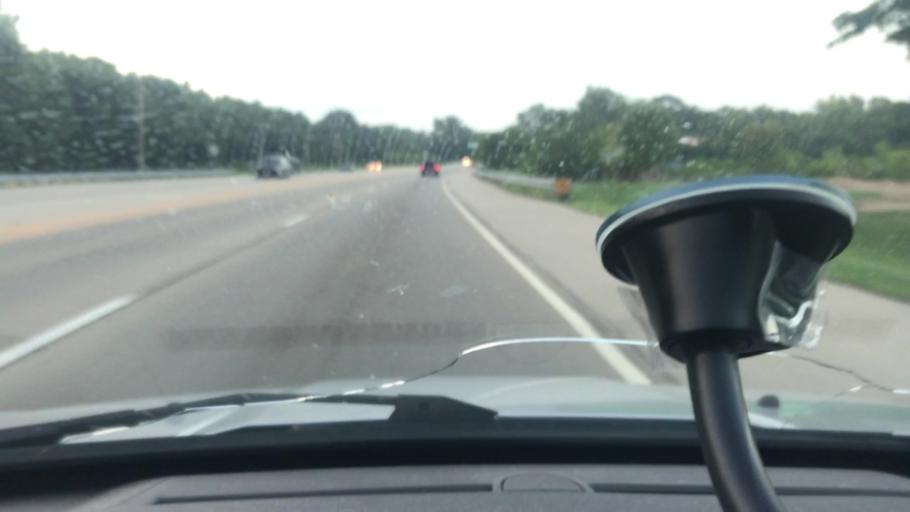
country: US
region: Illinois
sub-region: Tazewell County
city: North Pekin
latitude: 40.6096
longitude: -89.6342
